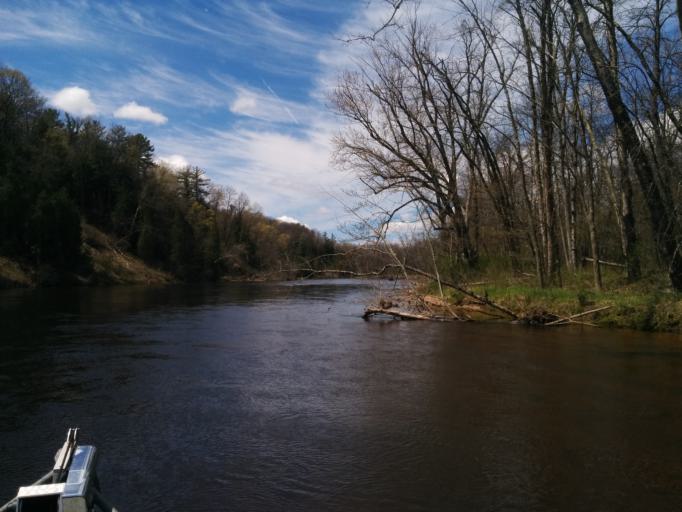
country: US
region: Michigan
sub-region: Newaygo County
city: Newaygo
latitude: 43.4069
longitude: -85.7183
